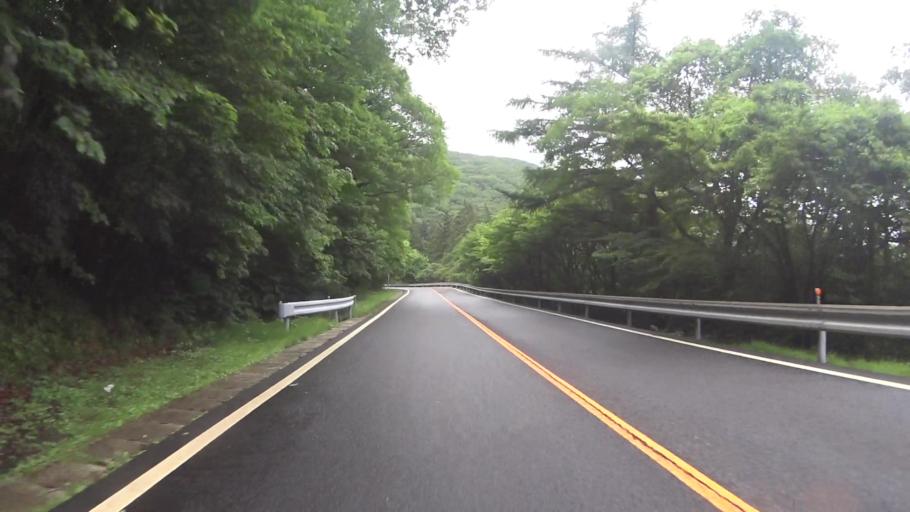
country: JP
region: Oita
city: Tsukawaki
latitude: 33.0997
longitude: 131.2224
